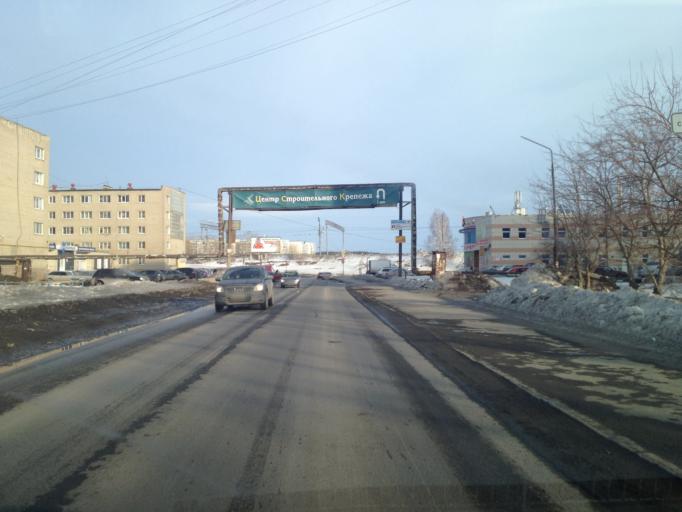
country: RU
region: Sverdlovsk
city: Sovkhoznyy
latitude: 56.7559
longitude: 60.6072
